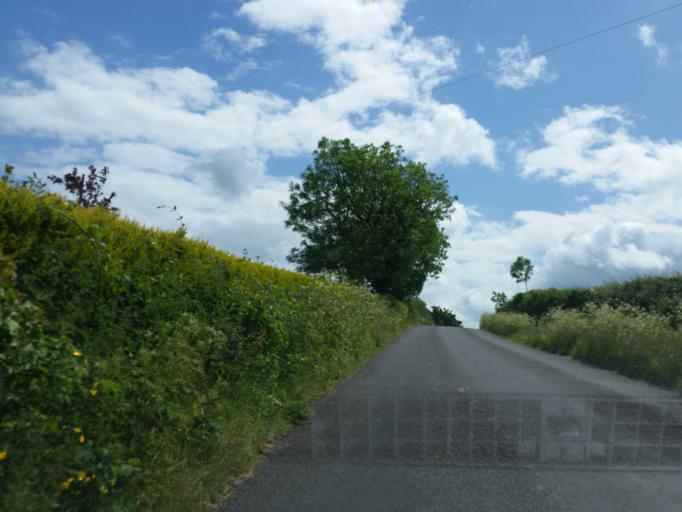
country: GB
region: Northern Ireland
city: Fivemiletown
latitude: 54.3580
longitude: -7.3049
